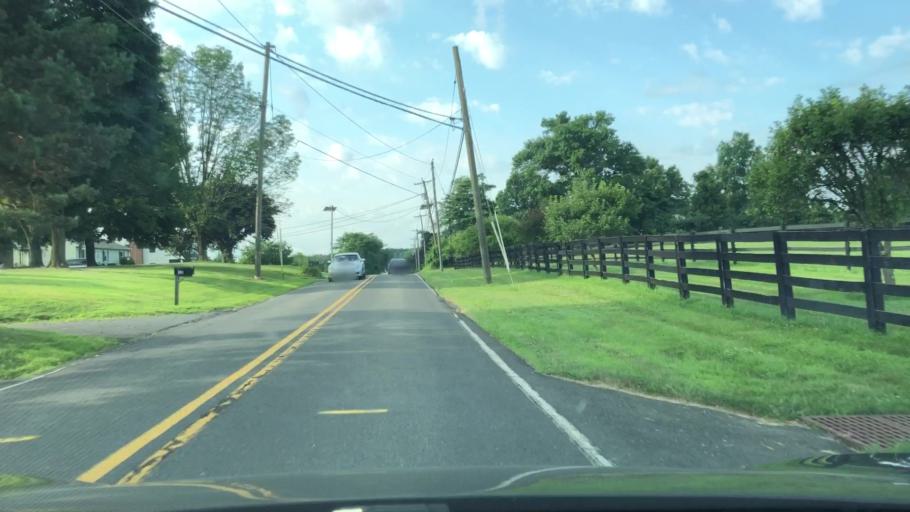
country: US
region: New Jersey
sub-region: Mercer County
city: Pennington
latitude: 40.3359
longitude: -74.8165
